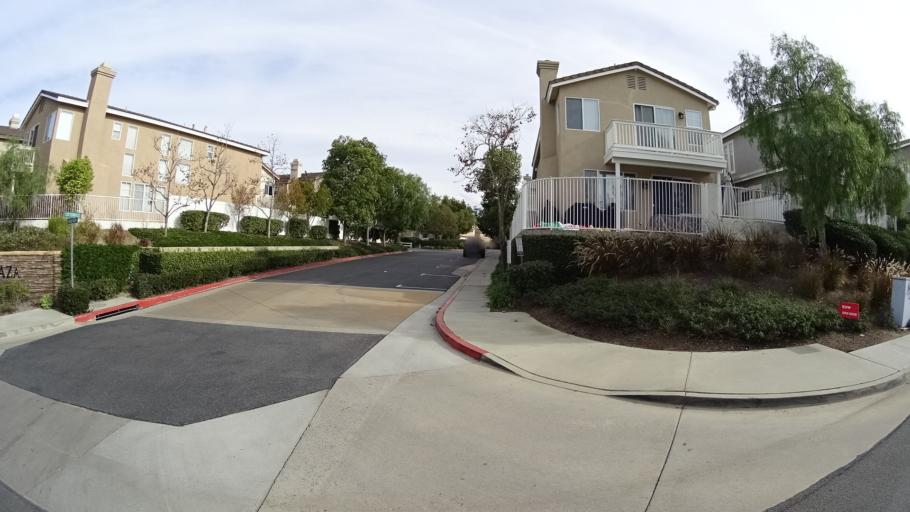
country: US
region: California
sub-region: Orange County
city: Aliso Viejo
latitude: 33.5855
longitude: -117.7388
